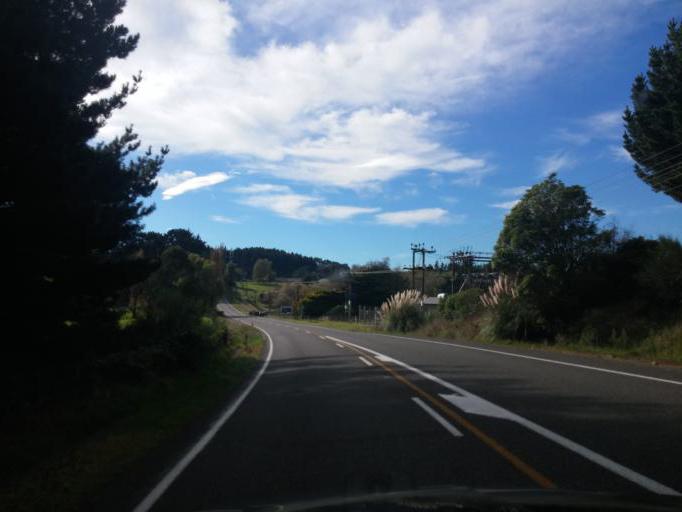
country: NZ
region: Manawatu-Wanganui
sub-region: Palmerston North City
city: Palmerston North
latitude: -40.3945
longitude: 175.6311
